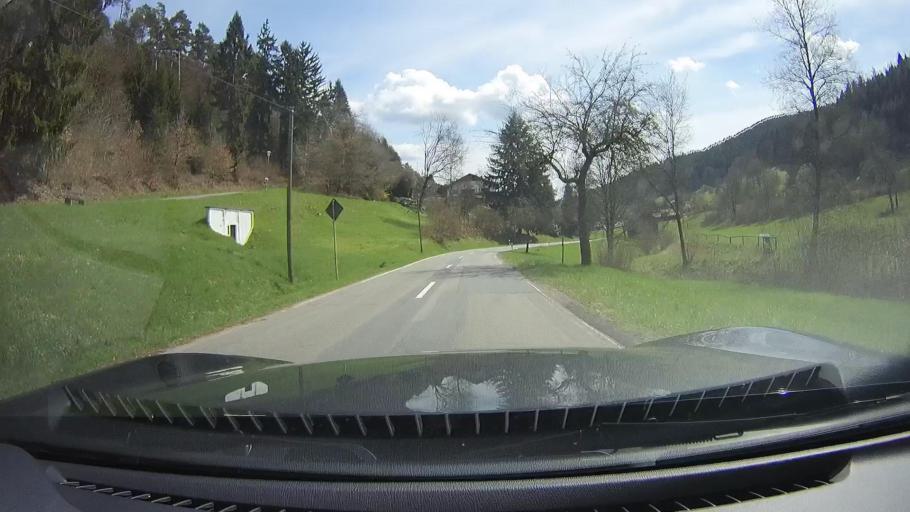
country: DE
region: Hesse
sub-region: Regierungsbezirk Darmstadt
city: Hesseneck
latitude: 49.5749
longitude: 9.0608
